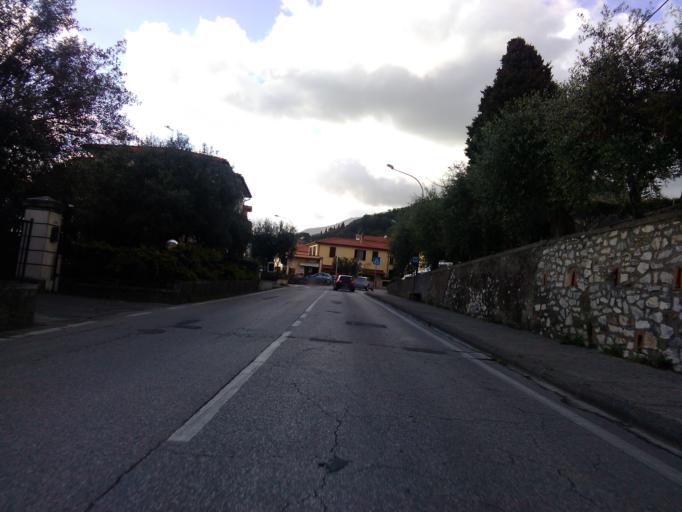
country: IT
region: Tuscany
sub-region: Provincia di Lucca
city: Seravezza
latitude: 43.9814
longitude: 10.2201
